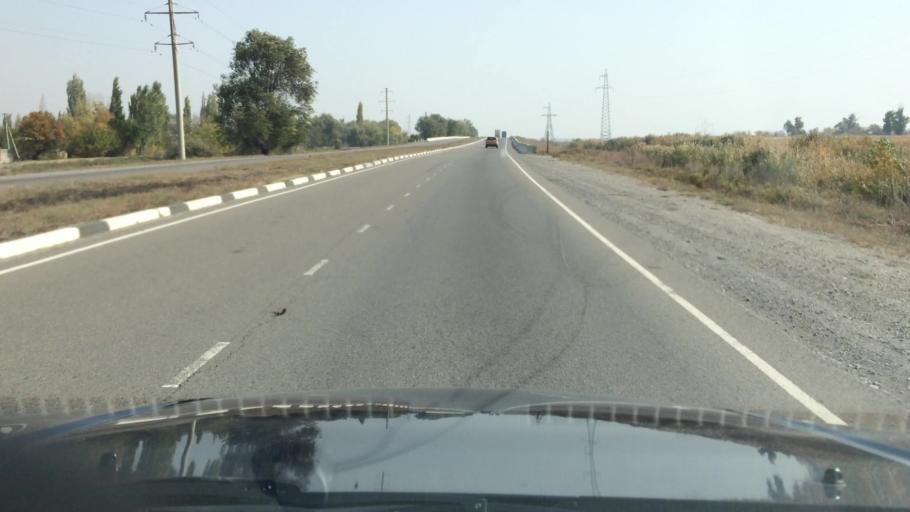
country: KG
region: Chuy
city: Kant
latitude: 42.9672
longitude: 74.8309
